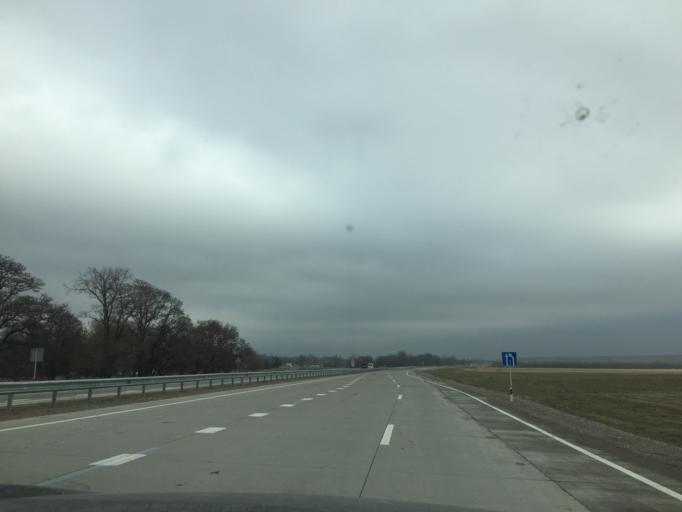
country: KZ
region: Ongtustik Qazaqstan
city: Kokterek
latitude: 42.5548
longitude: 70.1415
